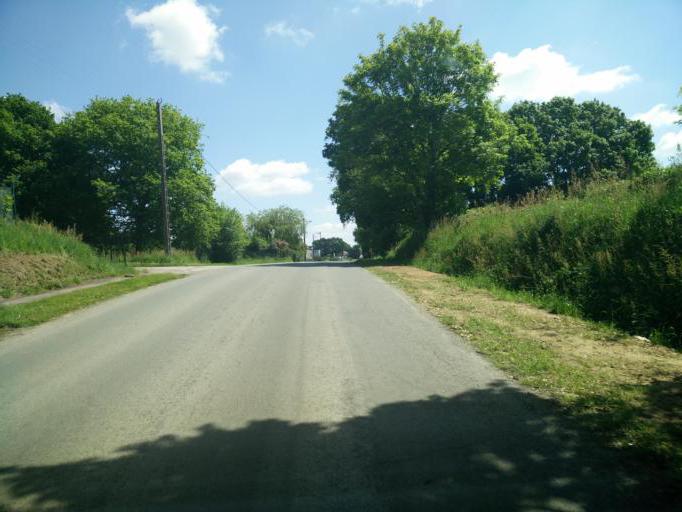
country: FR
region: Brittany
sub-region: Departement du Morbihan
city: Josselin
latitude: 47.9513
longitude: -2.5359
